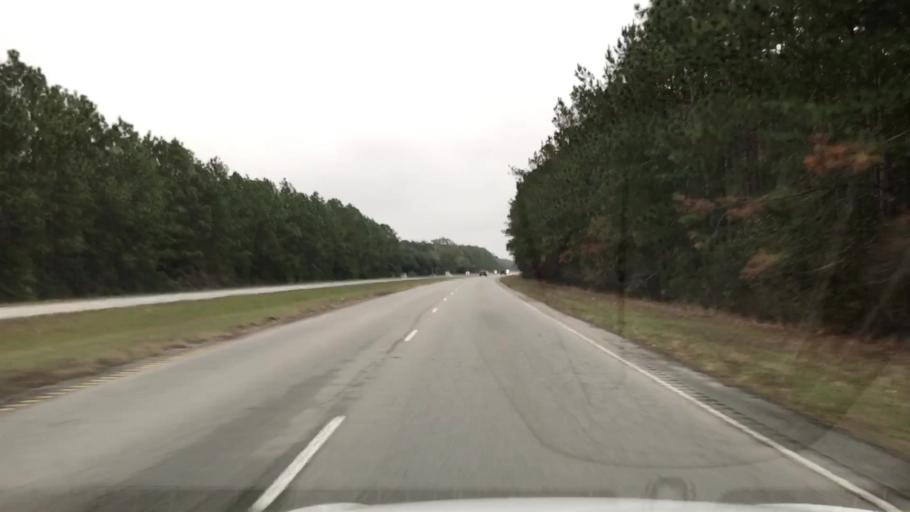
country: US
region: South Carolina
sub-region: Charleston County
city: Awendaw
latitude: 32.9798
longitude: -79.6620
